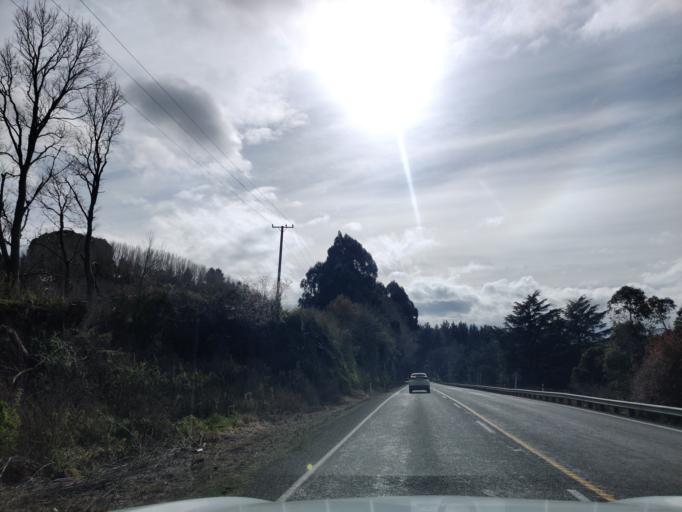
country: NZ
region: Manawatu-Wanganui
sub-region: Ruapehu District
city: Waiouru
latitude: -39.8845
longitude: 175.6718
